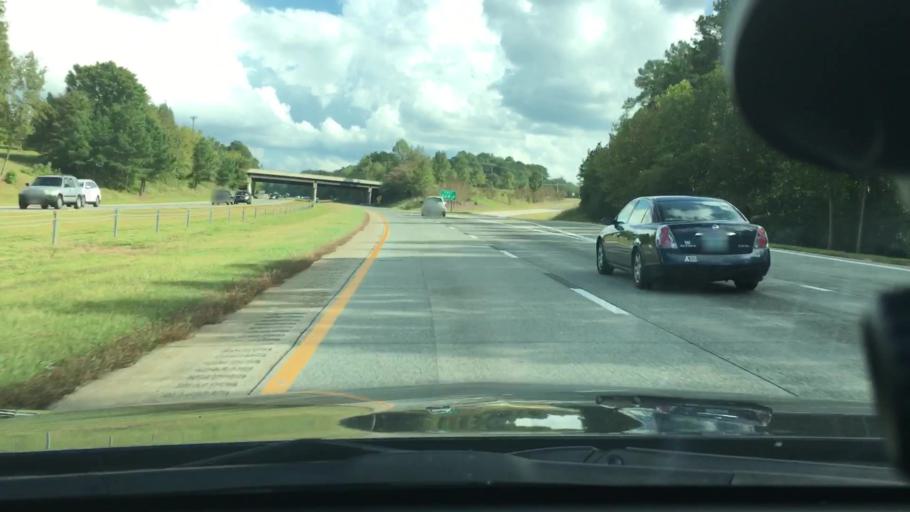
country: US
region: North Carolina
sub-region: Orange County
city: Chapel Hill
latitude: 35.9727
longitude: -79.0656
